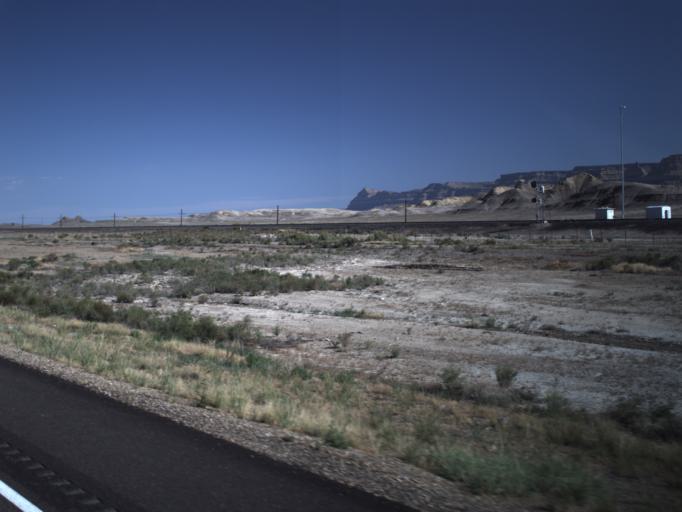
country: US
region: Utah
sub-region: Carbon County
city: East Carbon City
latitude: 39.0140
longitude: -110.2861
